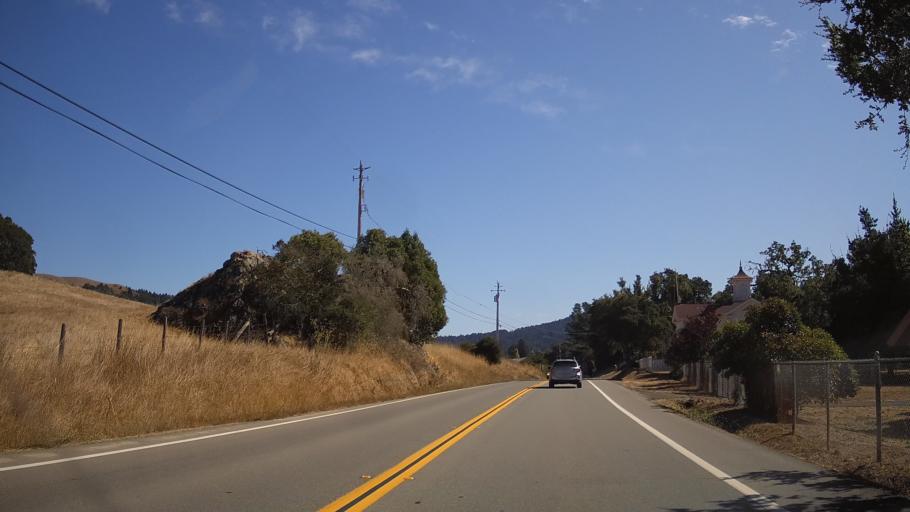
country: US
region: California
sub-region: Marin County
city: Lagunitas-Forest Knolls
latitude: 38.0685
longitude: -122.7036
